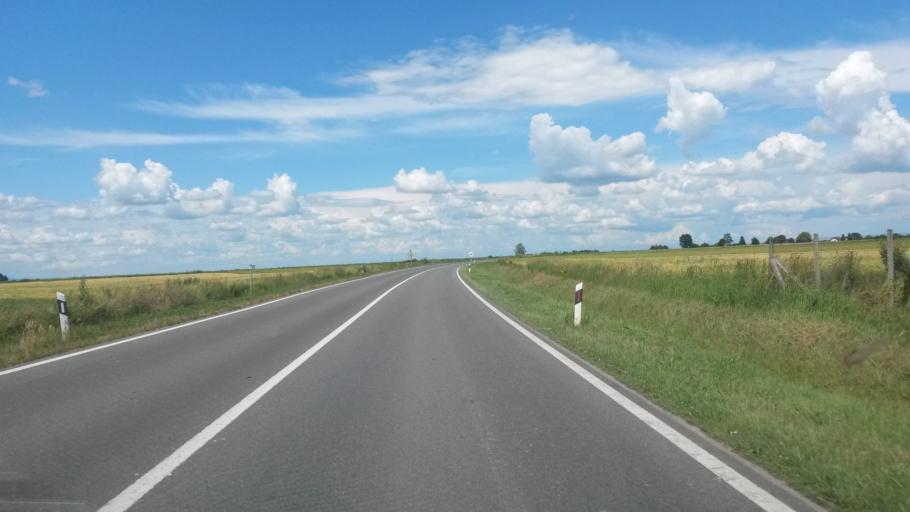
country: HR
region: Osjecko-Baranjska
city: Cepin
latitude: 45.5198
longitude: 18.5372
